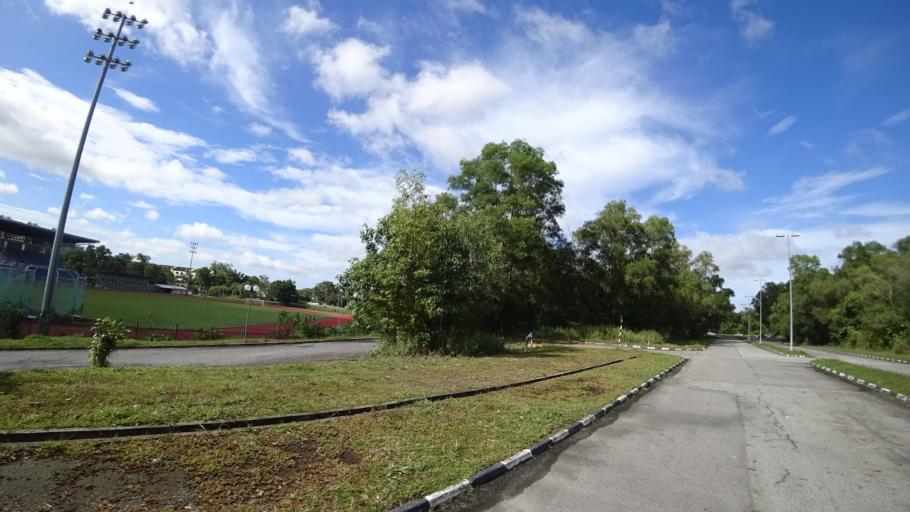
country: BN
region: Brunei and Muara
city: Bandar Seri Begawan
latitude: 4.9303
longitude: 114.9483
